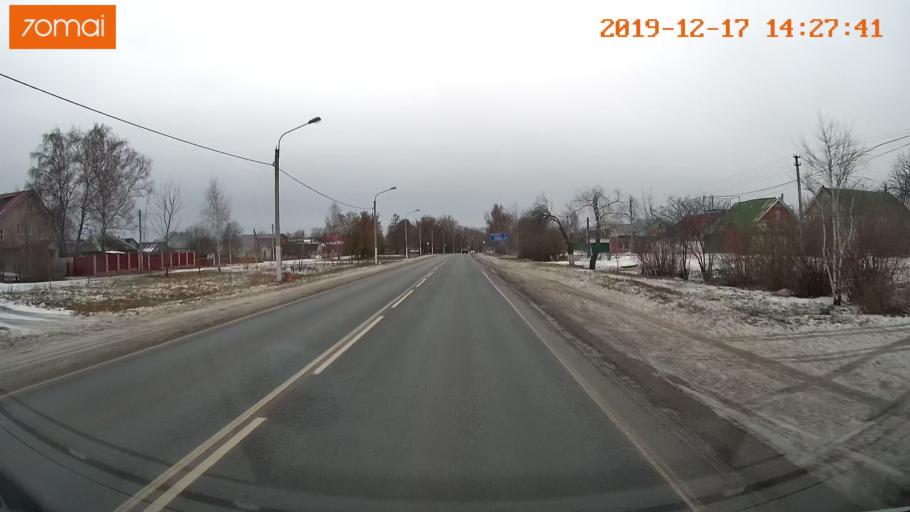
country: RU
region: Rjazan
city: Zakharovo
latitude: 54.3735
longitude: 39.2895
